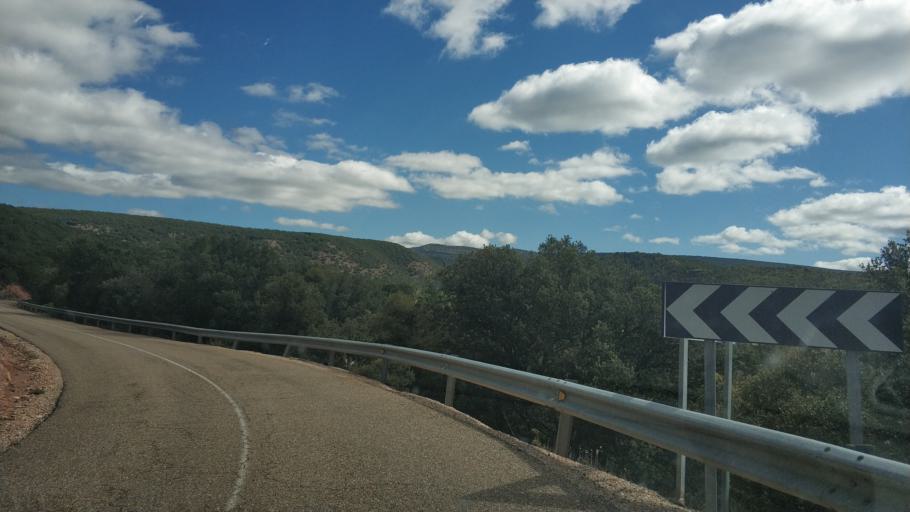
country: ES
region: Castille and Leon
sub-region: Provincia de Burgos
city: Retuerta
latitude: 42.0414
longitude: -3.4916
